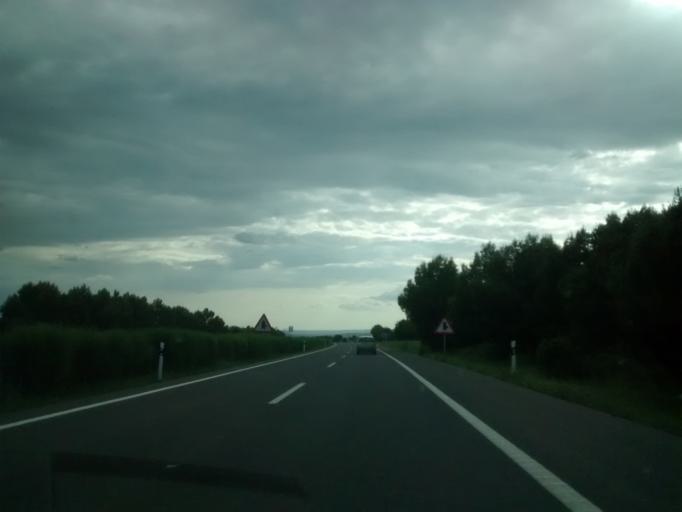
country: ES
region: Aragon
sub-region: Provincia de Huesca
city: Almudebar
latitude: 42.0664
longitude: -0.5211
